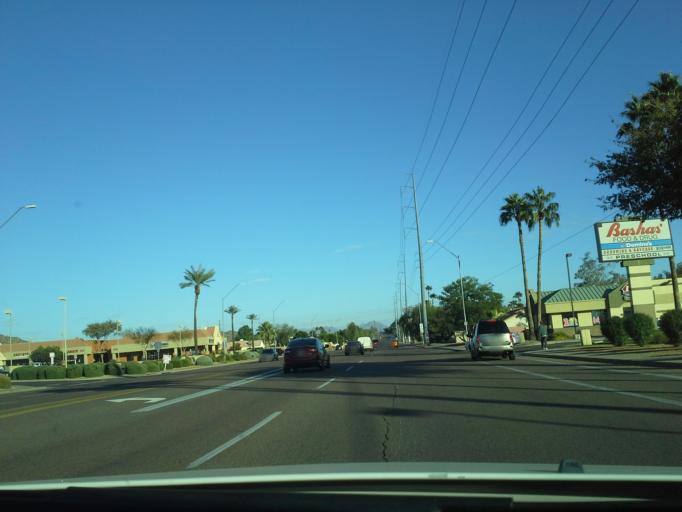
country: US
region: Arizona
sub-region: Maricopa County
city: Glendale
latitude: 33.6547
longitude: -112.0643
